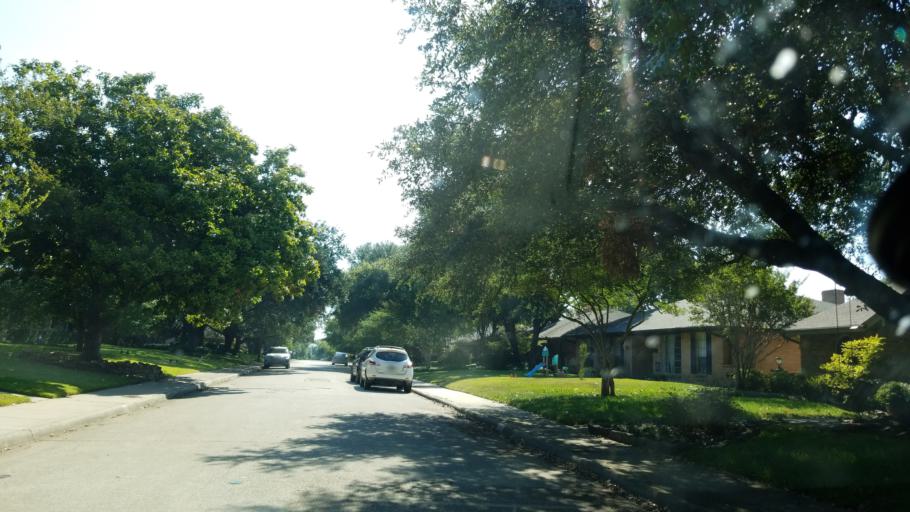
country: US
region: Texas
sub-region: Dallas County
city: Richardson
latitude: 32.9040
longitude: -96.7351
